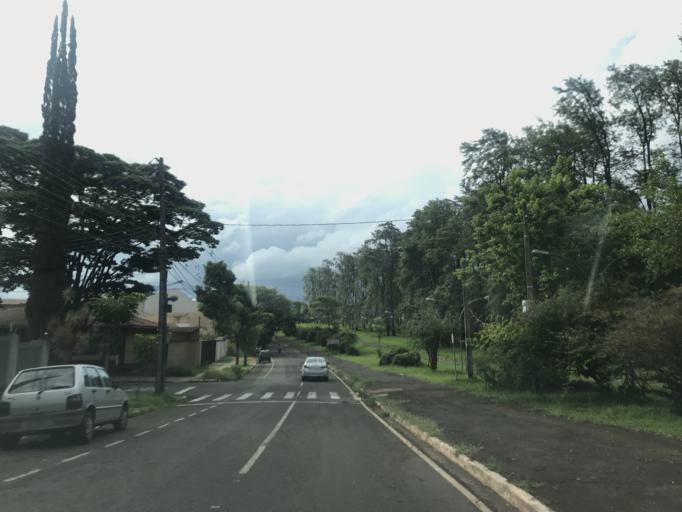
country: BR
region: Parana
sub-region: Maringa
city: Maringa
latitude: -23.4280
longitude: -51.9622
